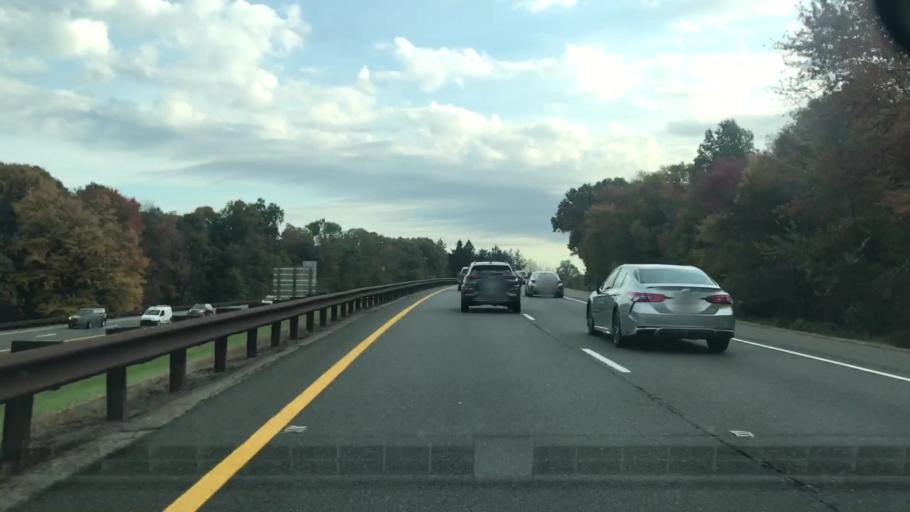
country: US
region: New Jersey
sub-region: Bergen County
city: Woodcliff Lake
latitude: 41.0176
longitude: -74.0680
